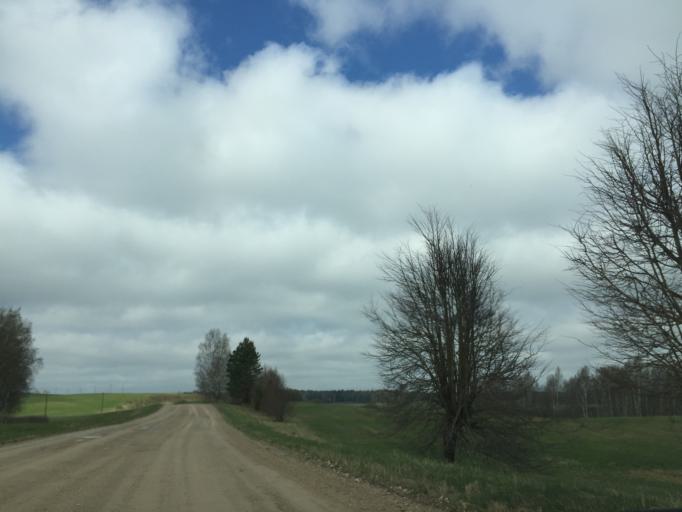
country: EE
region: Valgamaa
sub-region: Valga linn
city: Valga
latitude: 57.5665
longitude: 26.2613
